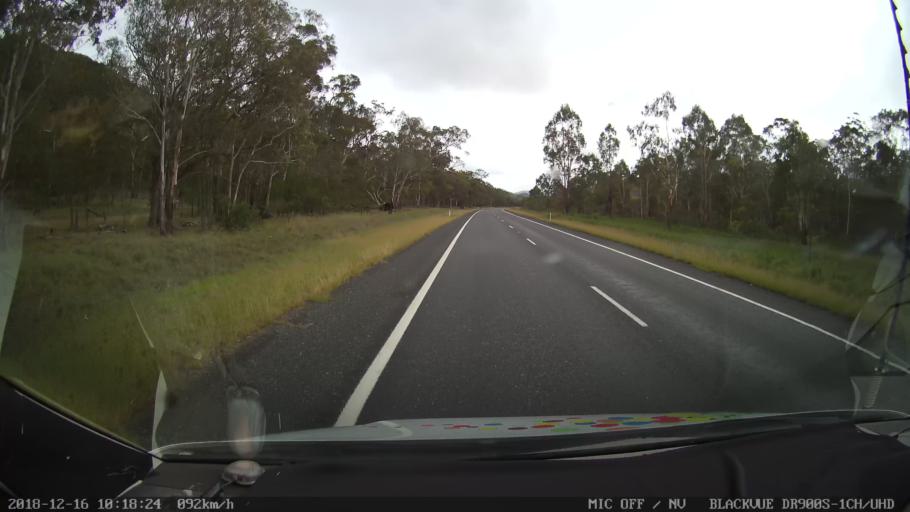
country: AU
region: New South Wales
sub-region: Tenterfield Municipality
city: Carrolls Creek
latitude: -29.2440
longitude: 151.9975
